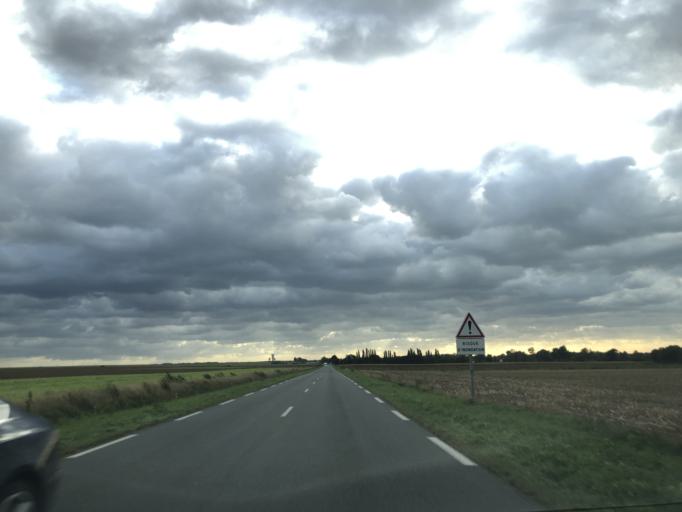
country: FR
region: Picardie
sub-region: Departement de la Somme
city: Pende
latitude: 50.1506
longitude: 1.5455
